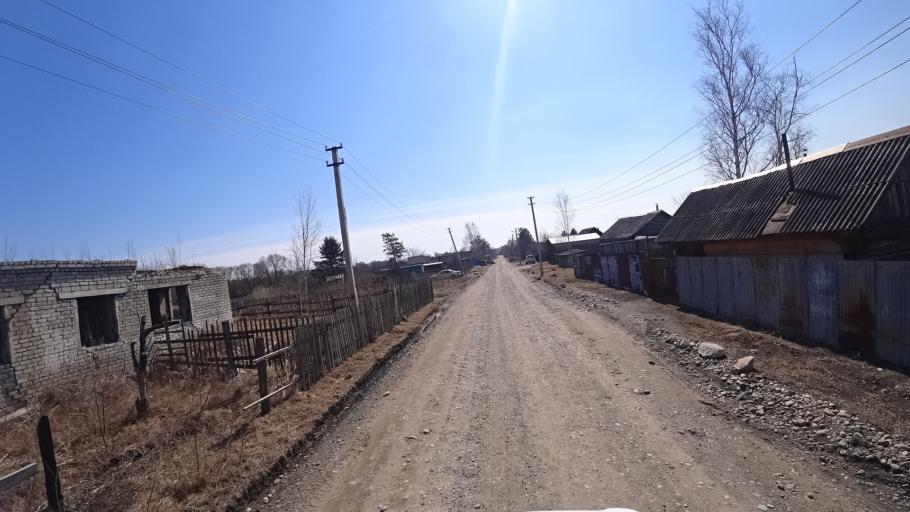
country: RU
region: Amur
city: Novobureyskiy
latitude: 49.7910
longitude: 129.8524
